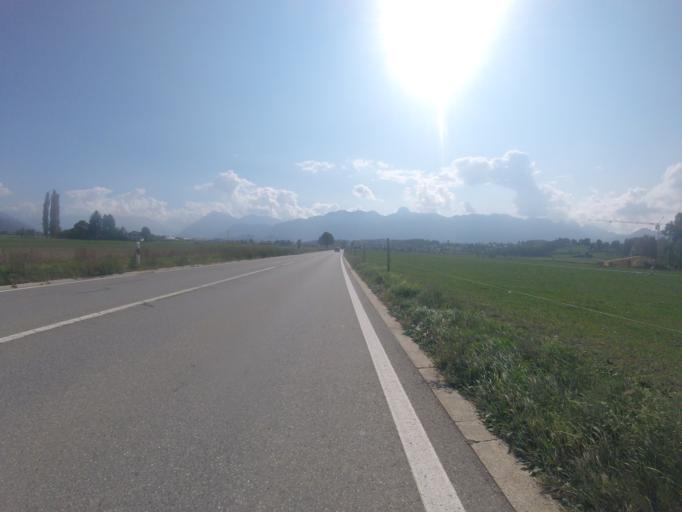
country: CH
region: Bern
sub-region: Thun District
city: Uttigen
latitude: 46.7851
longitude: 7.5741
